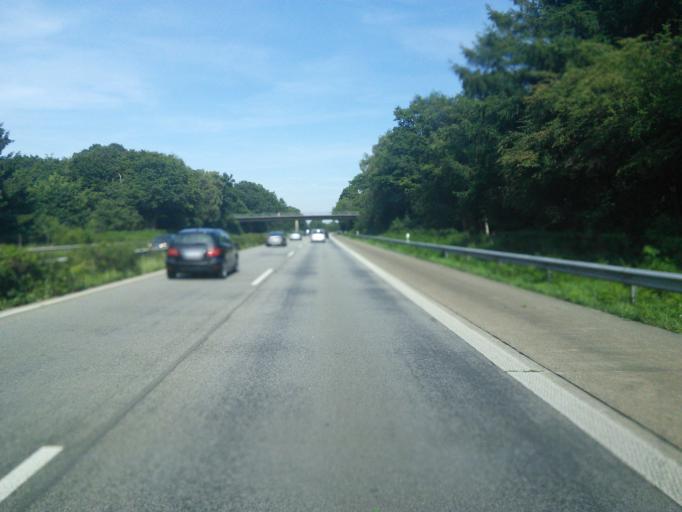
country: DE
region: North Rhine-Westphalia
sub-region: Regierungsbezirk Dusseldorf
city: Kaarst
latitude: 51.2348
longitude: 6.5894
